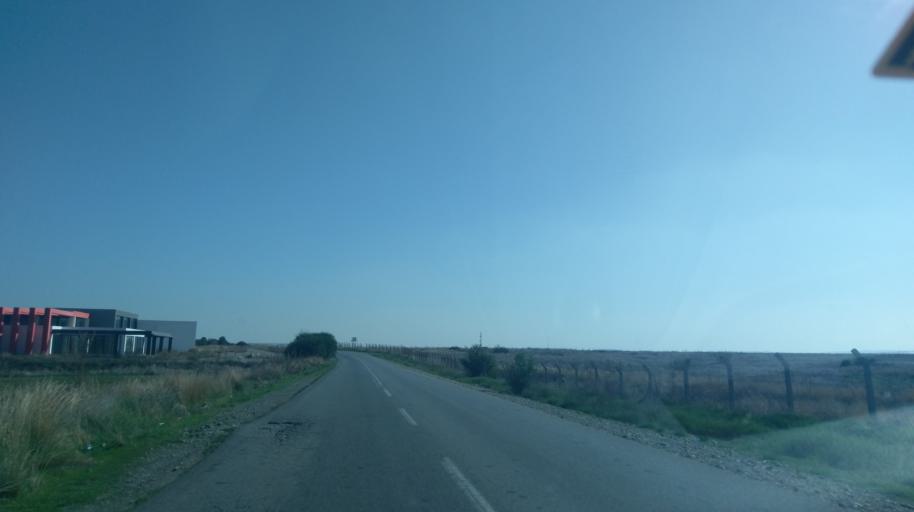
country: CY
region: Larnaka
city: Athienou
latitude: 35.1567
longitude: 33.5088
